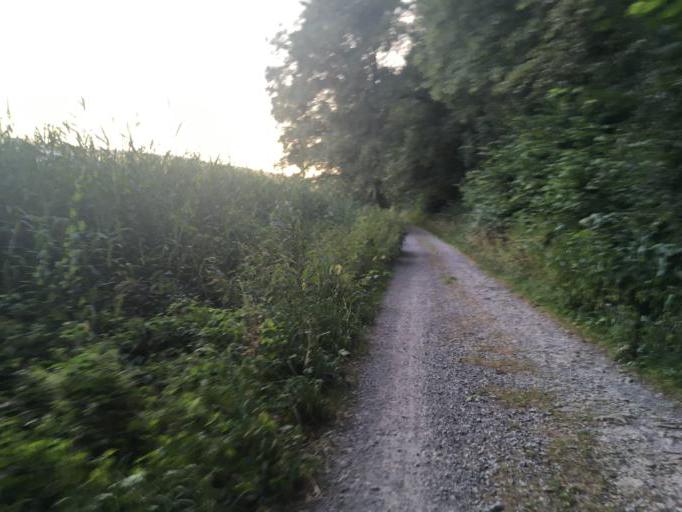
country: DE
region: Baden-Wuerttemberg
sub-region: Tuebingen Region
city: Kusterdingen
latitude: 48.5148
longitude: 9.0896
